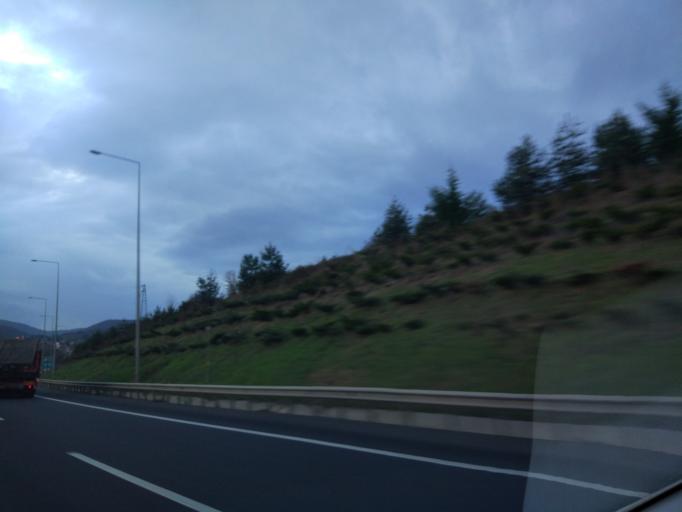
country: TR
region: Duzce
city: Kaynasli
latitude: 40.7240
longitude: 31.4536
